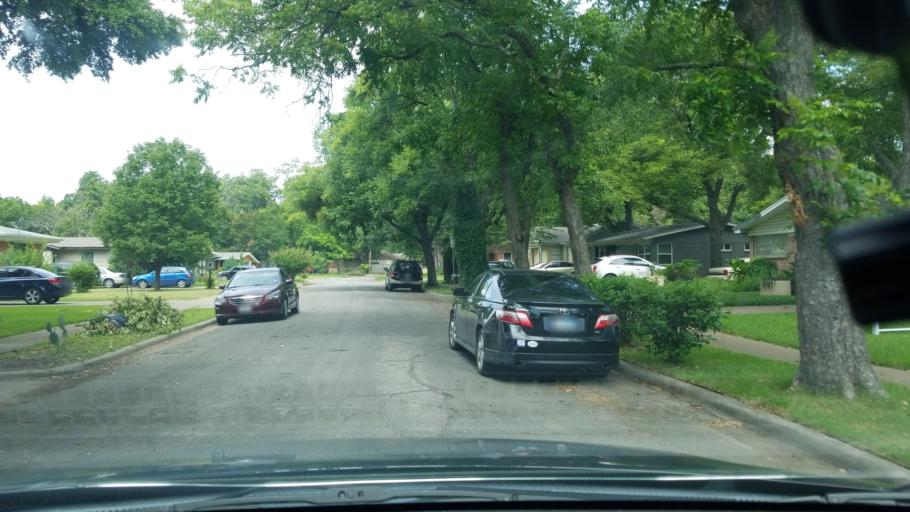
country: US
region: Texas
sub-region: Dallas County
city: Garland
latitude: 32.8300
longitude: -96.6767
